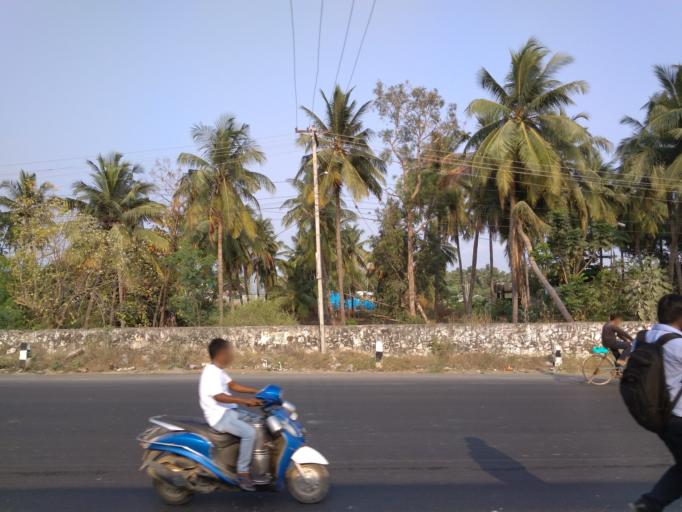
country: IN
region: Tamil Nadu
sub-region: Kancheepuram
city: Injambakkam
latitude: 12.8249
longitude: 80.2314
